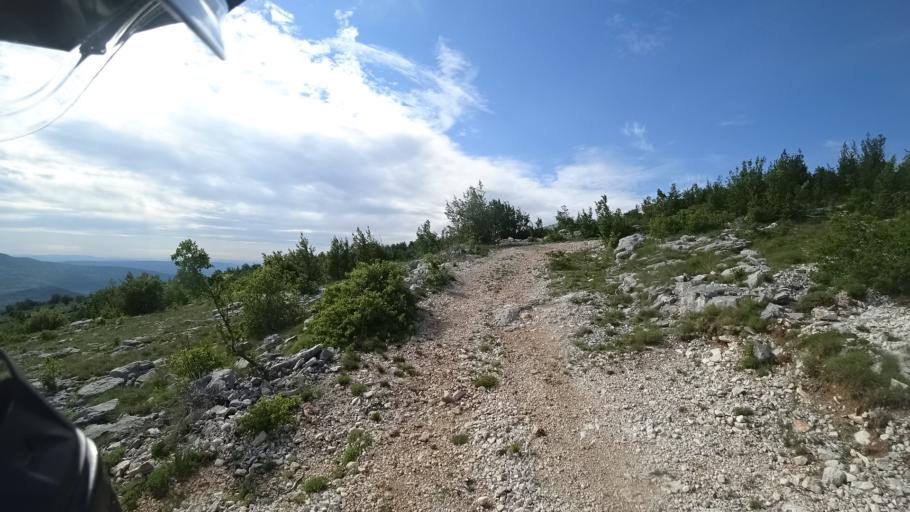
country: HR
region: Splitsko-Dalmatinska
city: Hrvace
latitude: 43.7885
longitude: 16.4334
